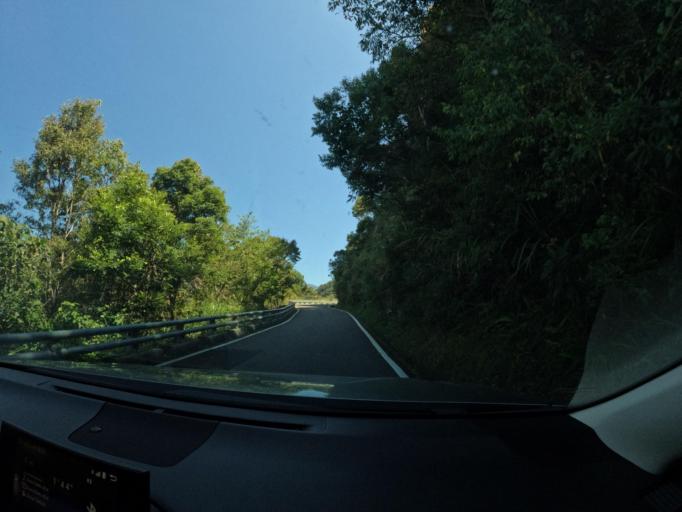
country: TW
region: Taiwan
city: Yujing
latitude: 23.2855
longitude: 120.8446
